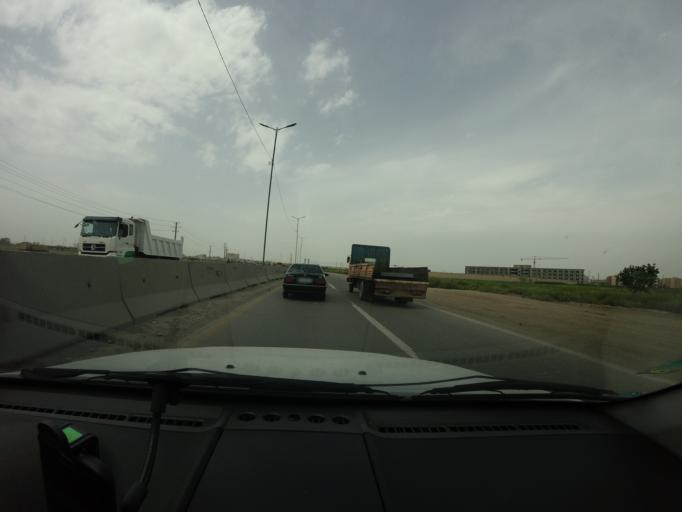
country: IR
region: Tehran
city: Eslamshahr
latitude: 35.5143
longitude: 51.2375
